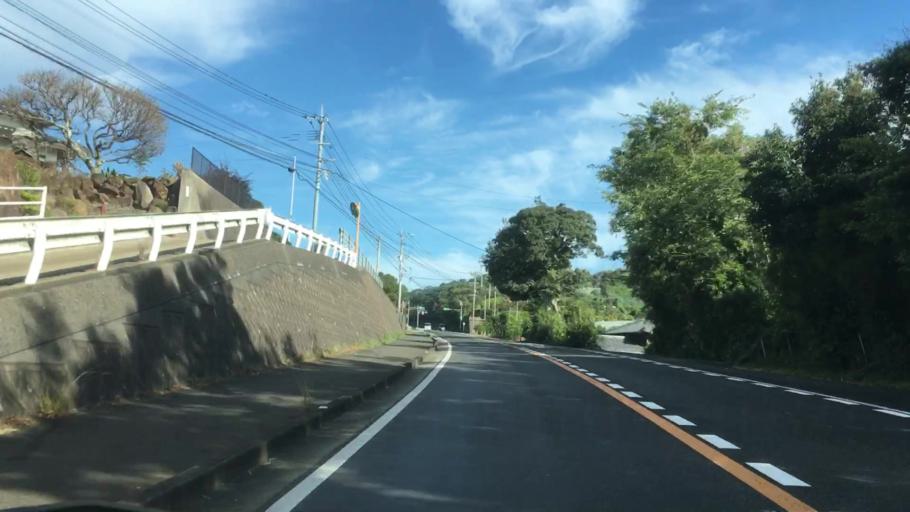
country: JP
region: Nagasaki
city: Sasebo
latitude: 33.0822
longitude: 129.7559
